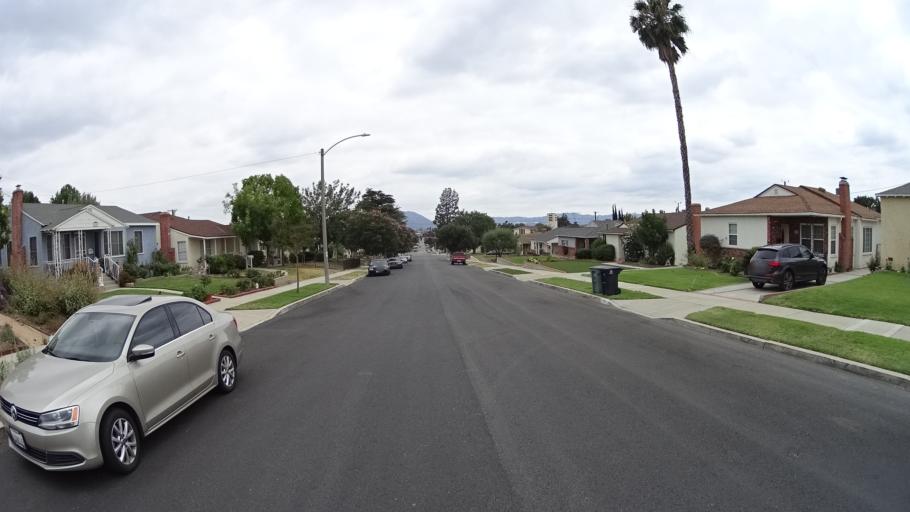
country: US
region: California
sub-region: Los Angeles County
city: Burbank
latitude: 34.2040
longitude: -118.3335
